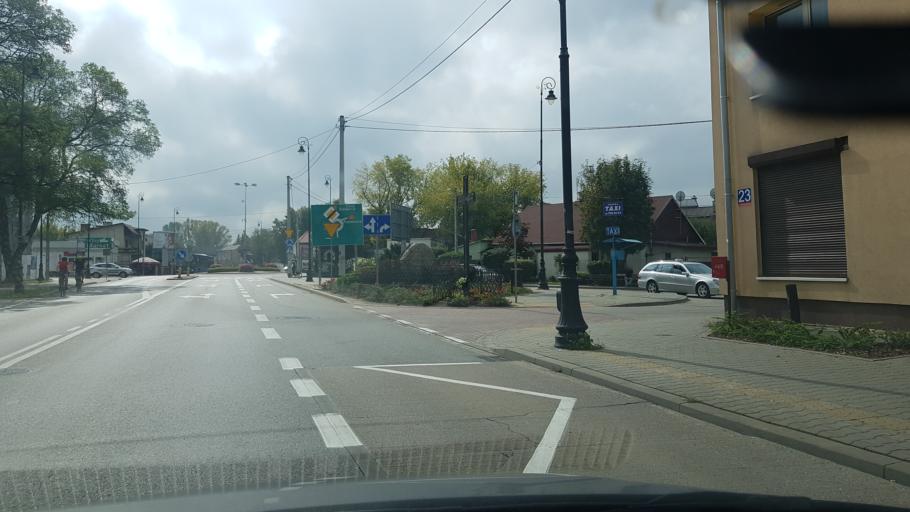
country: PL
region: Masovian Voivodeship
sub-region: Powiat piaseczynski
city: Konstancin-Jeziorna
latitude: 52.0948
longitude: 21.1174
